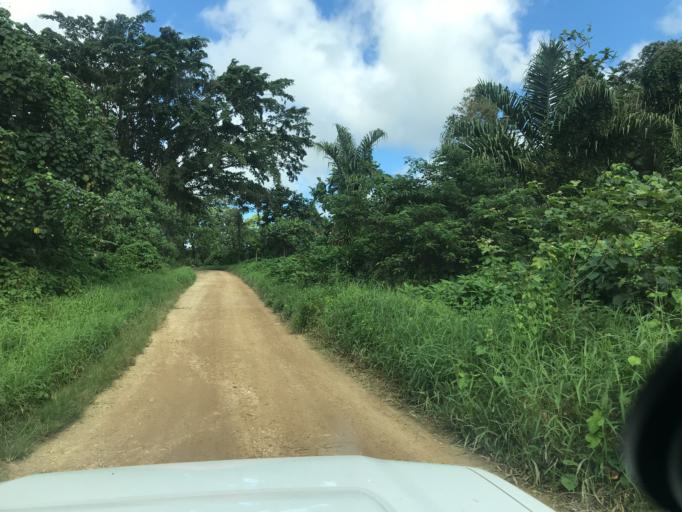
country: VU
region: Sanma
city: Luganville
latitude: -15.4734
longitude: 167.0775
